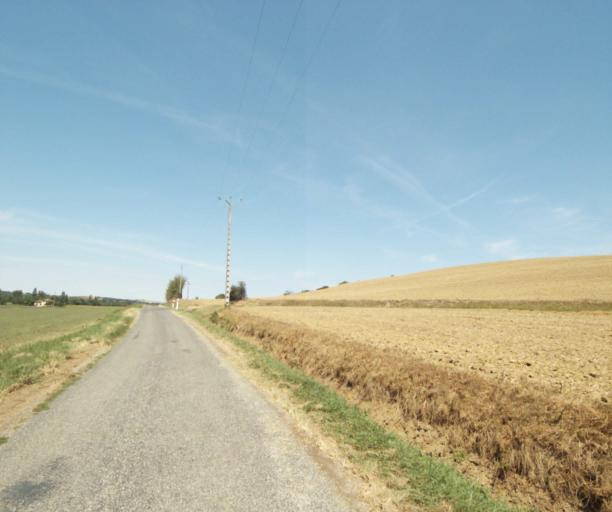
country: FR
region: Midi-Pyrenees
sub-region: Departement de la Haute-Garonne
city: Saint-Sulpice-sur-Leze
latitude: 43.3142
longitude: 1.3375
